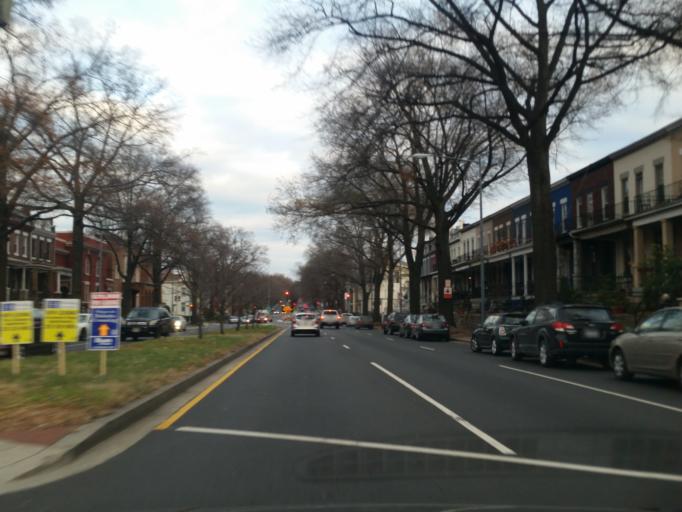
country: US
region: Washington, D.C.
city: Washington, D.C.
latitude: 38.9144
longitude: -77.0157
